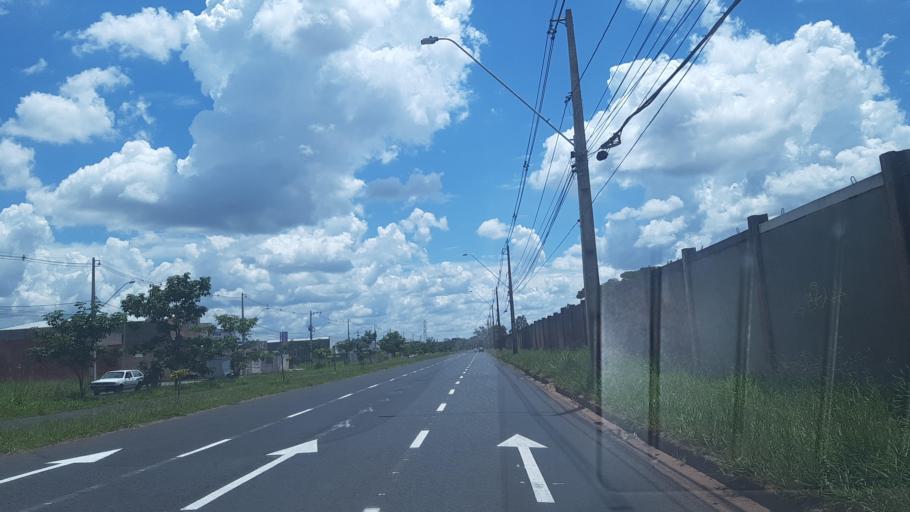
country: BR
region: Minas Gerais
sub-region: Uberlandia
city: Uberlandia
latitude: -18.9621
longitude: -48.3397
